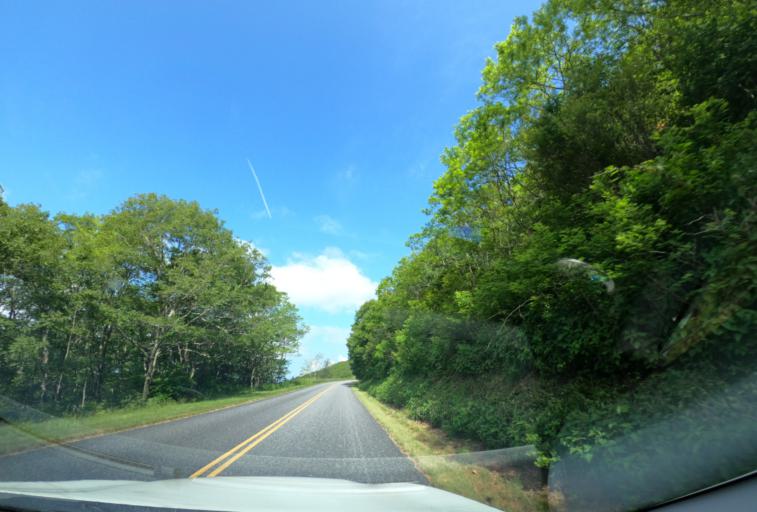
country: US
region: North Carolina
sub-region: Haywood County
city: Hazelwood
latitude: 35.3877
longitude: -83.0324
